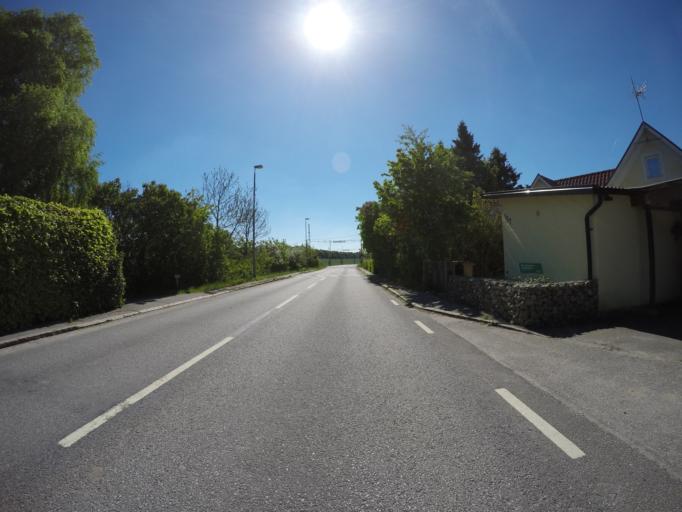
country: SE
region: Skane
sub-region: Malmo
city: Oxie
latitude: 55.5381
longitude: 13.1264
